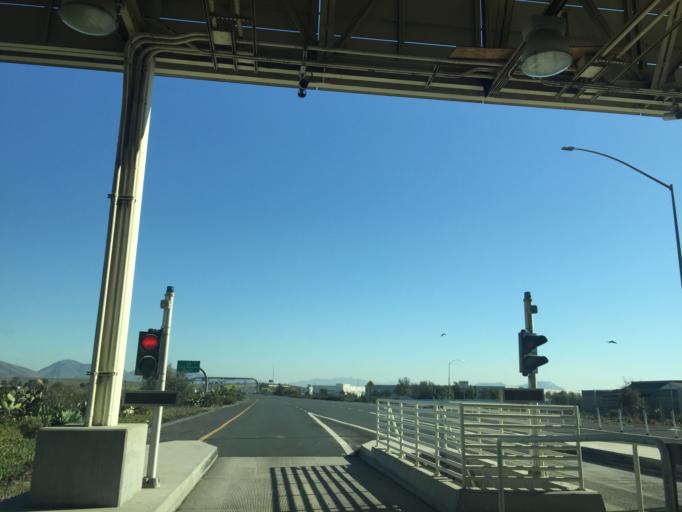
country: MX
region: Baja California
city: Tijuana
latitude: 32.5776
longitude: -116.9592
